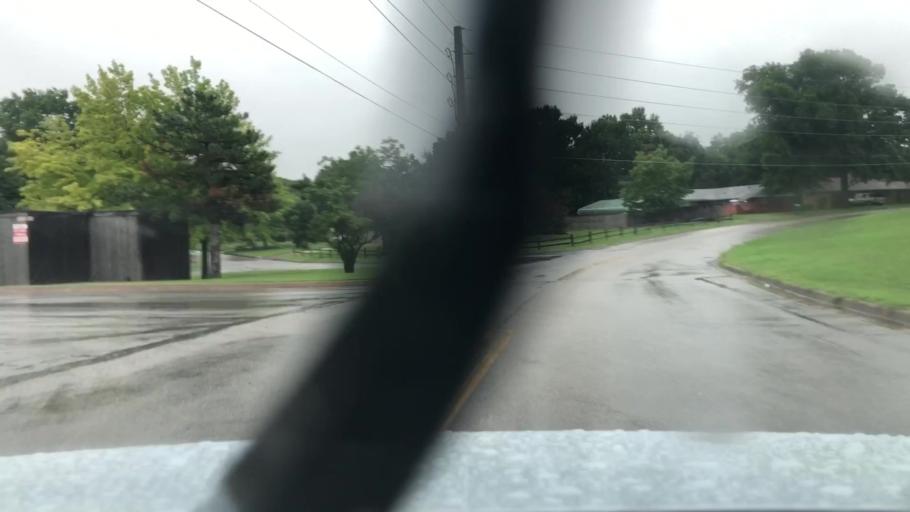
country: US
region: Oklahoma
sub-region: Washington County
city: Bartlesville
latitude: 36.7385
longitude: -95.9314
